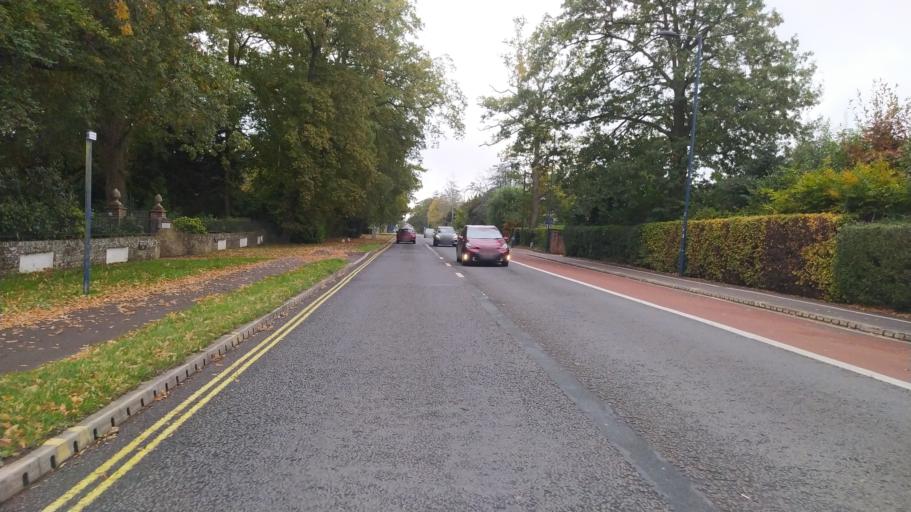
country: GB
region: England
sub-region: Hampshire
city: Cowplain
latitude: 50.9061
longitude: -1.0102
